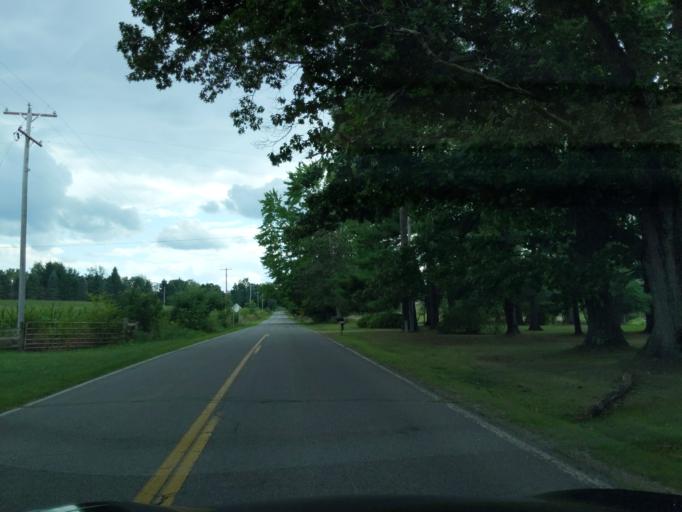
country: US
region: Michigan
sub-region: Ingham County
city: Leslie
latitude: 42.3717
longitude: -84.5444
